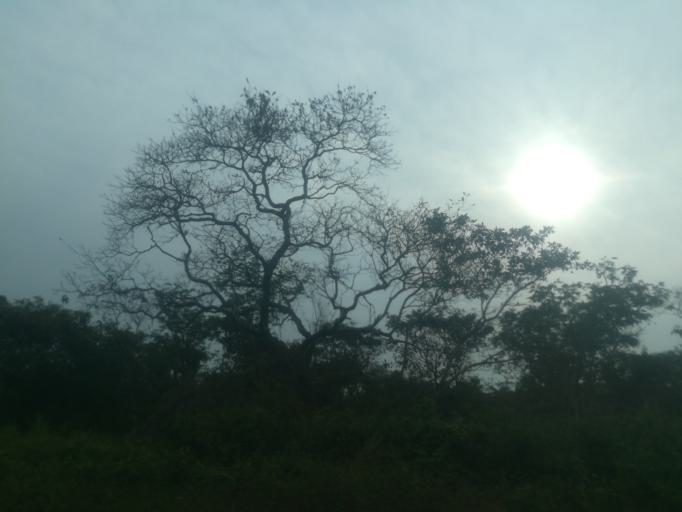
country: NG
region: Ogun
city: Ayetoro
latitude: 7.2767
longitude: 3.0965
